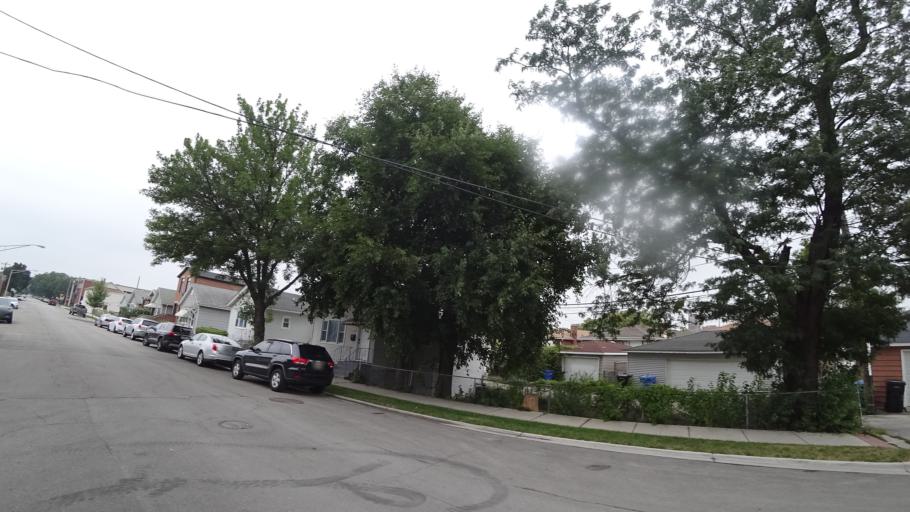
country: US
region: Illinois
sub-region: Cook County
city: Chicago
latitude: 41.8461
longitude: -87.6545
